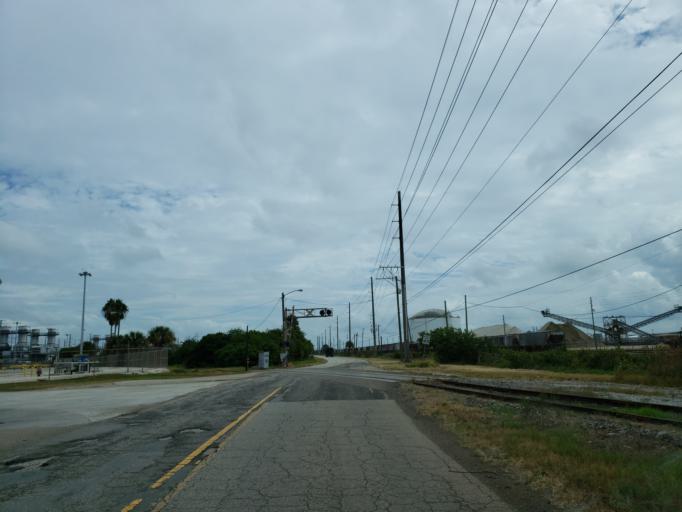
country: US
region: Florida
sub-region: Hillsborough County
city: Palm River-Clair Mel
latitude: 27.9064
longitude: -82.4164
